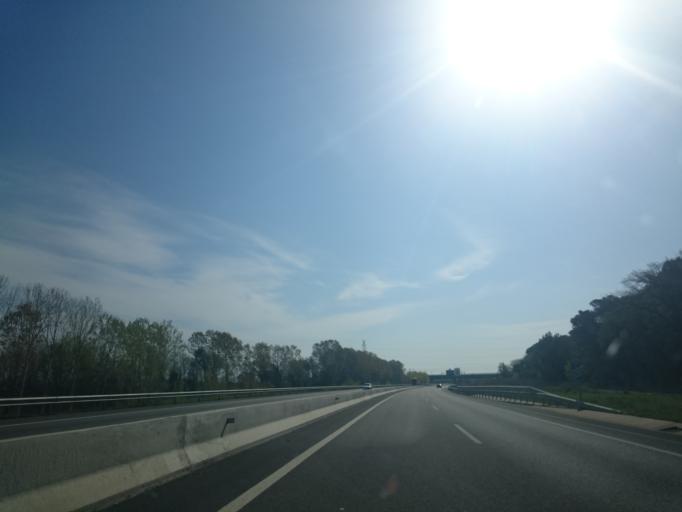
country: ES
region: Catalonia
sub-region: Provincia de Girona
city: Vilobi d'Onyar
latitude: 41.8754
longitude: 2.7532
